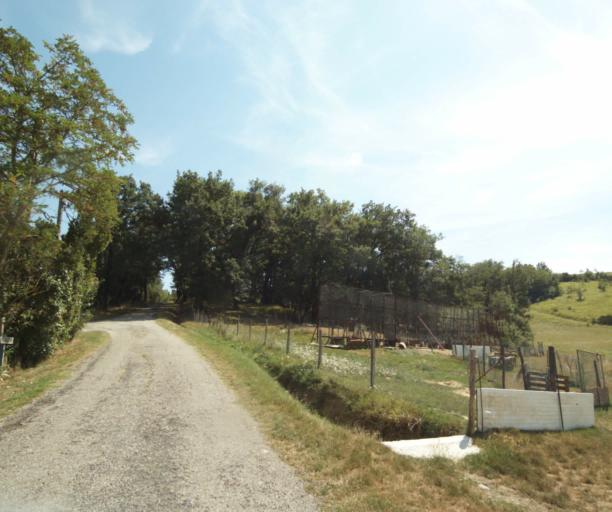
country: FR
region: Midi-Pyrenees
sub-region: Departement de l'Ariege
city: Lezat-sur-Leze
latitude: 43.2509
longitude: 1.3800
